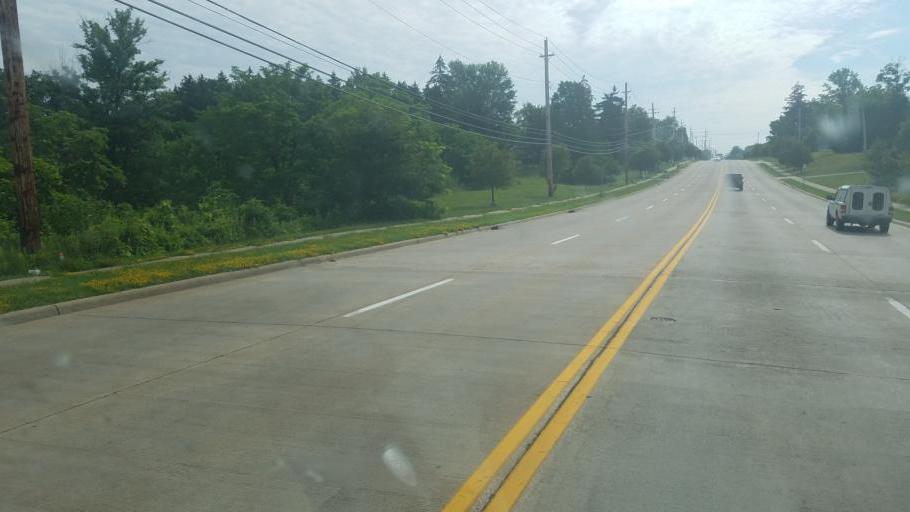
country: US
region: Ohio
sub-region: Cuyahoga County
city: Strongsville
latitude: 41.3123
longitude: -81.8687
